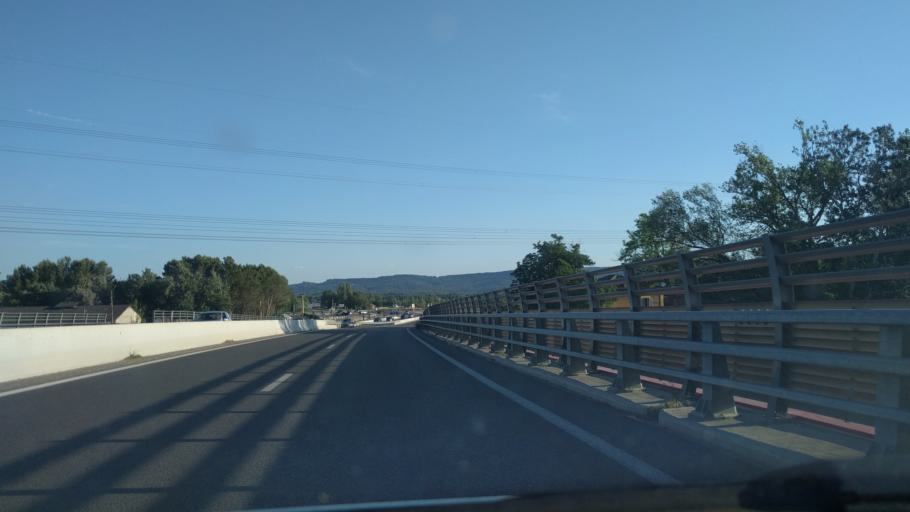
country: FR
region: Provence-Alpes-Cote d'Azur
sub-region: Departement du Vaucluse
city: Pertuis
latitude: 43.6663
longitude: 5.4962
